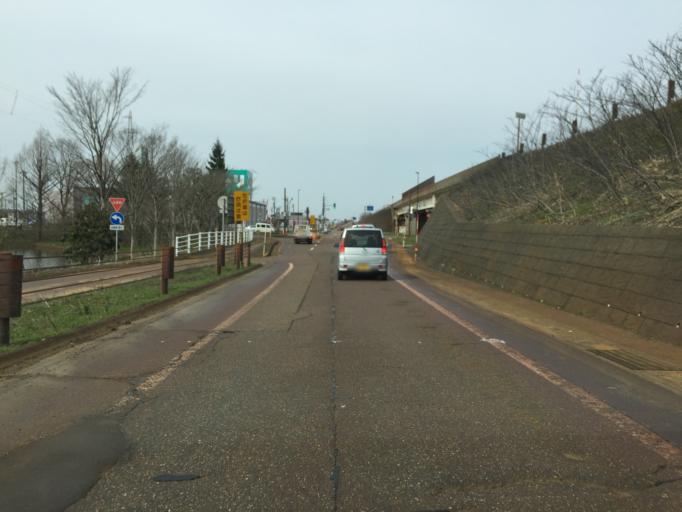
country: JP
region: Niigata
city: Nagaoka
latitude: 37.4557
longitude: 138.8771
